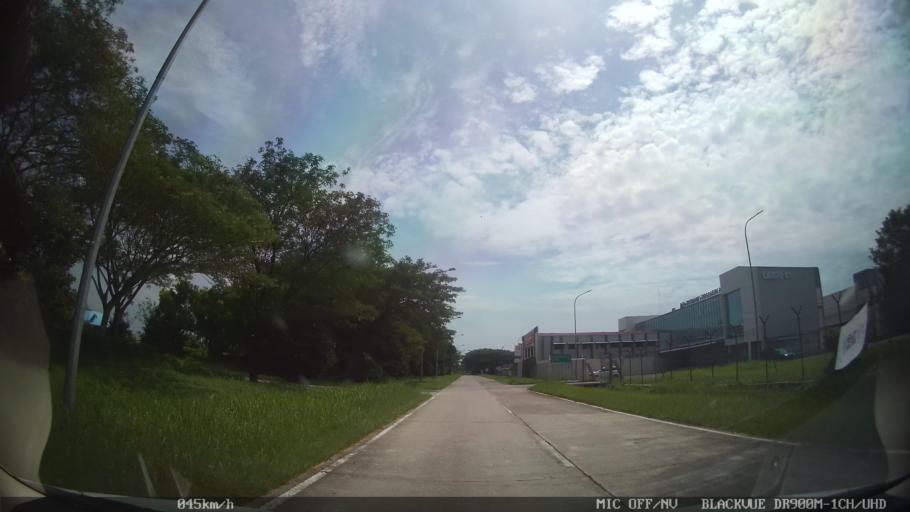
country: ID
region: North Sumatra
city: Percut
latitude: 3.6248
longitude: 98.8661
